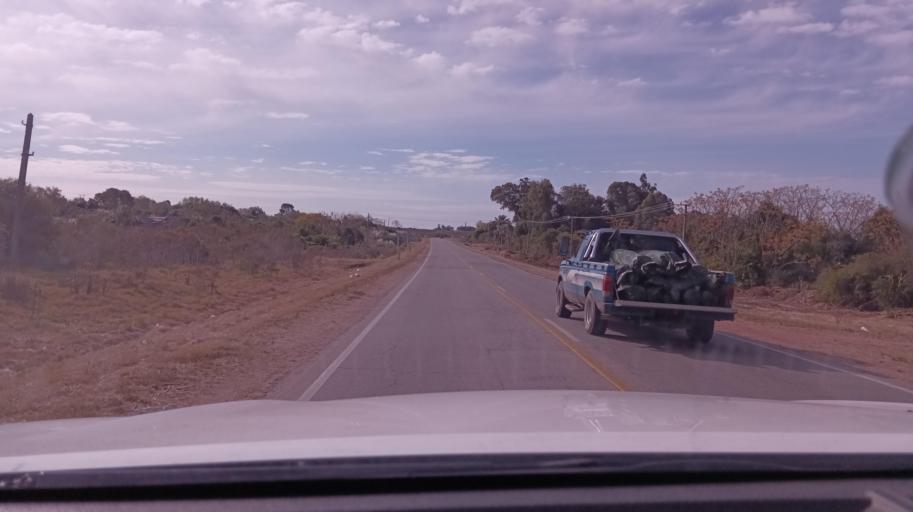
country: UY
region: Canelones
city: Toledo
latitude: -34.7147
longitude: -56.1127
